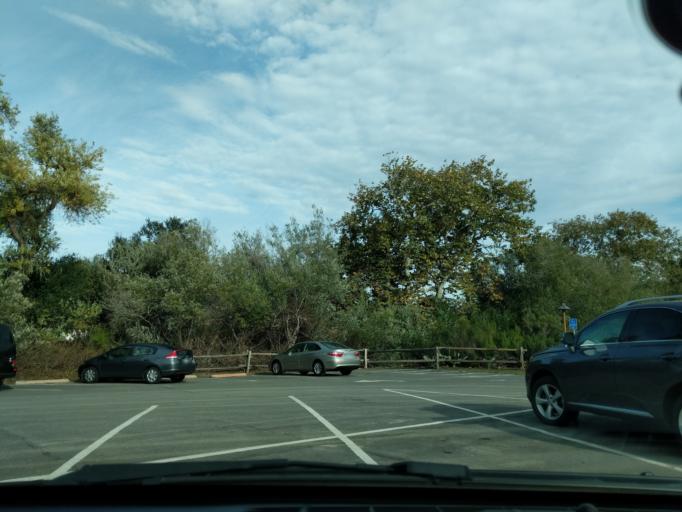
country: US
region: California
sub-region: Santa Barbara County
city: Mission Hills
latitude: 34.6702
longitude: -120.4211
